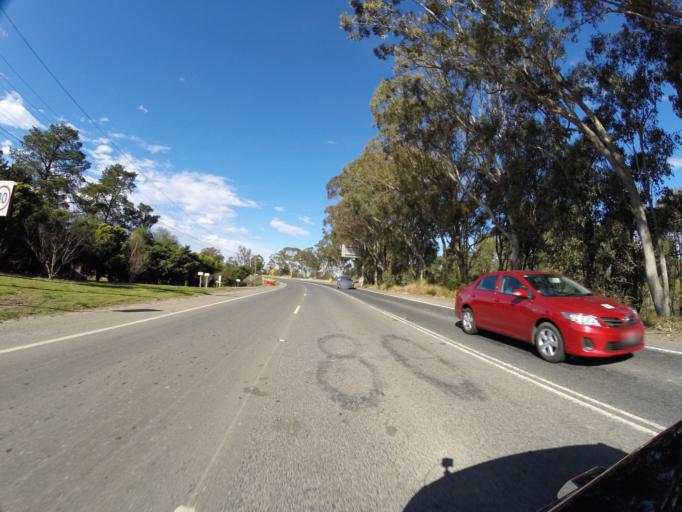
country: AU
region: New South Wales
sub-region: Fairfield
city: Cecil Park
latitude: -33.8804
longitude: 150.8187
